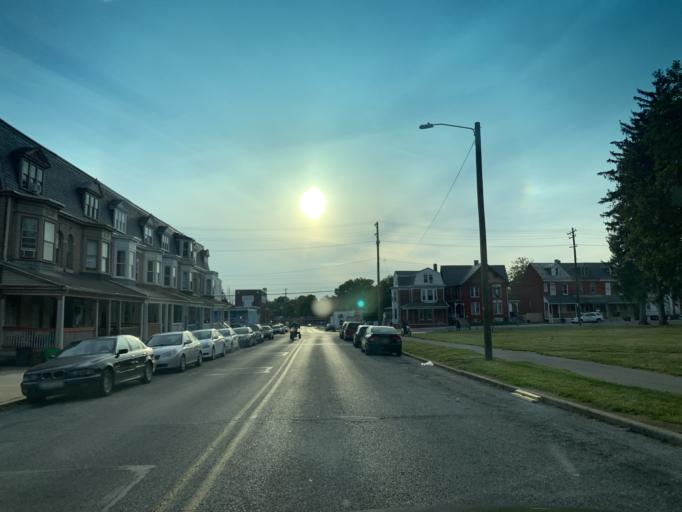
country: US
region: Pennsylvania
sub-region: York County
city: York
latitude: 39.9552
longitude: -76.7275
